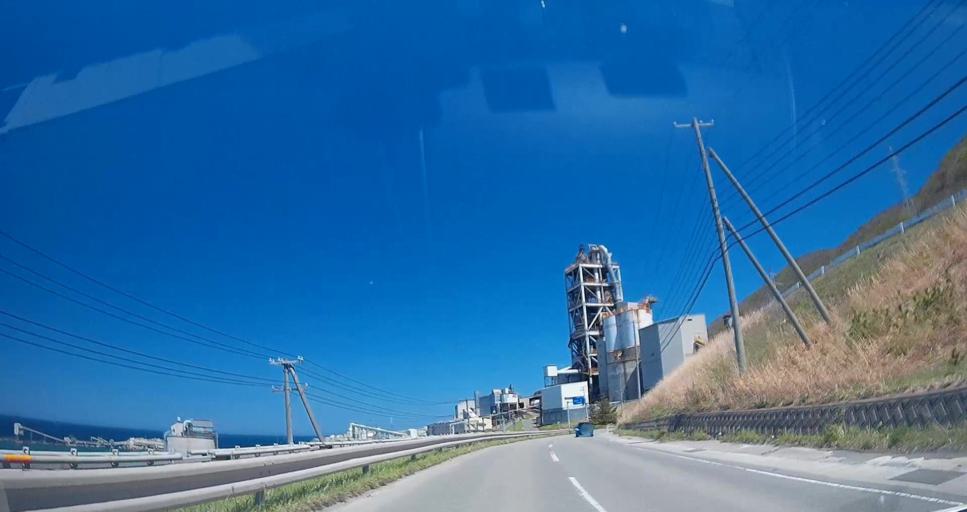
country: JP
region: Aomori
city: Mutsu
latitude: 41.4053
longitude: 141.4339
